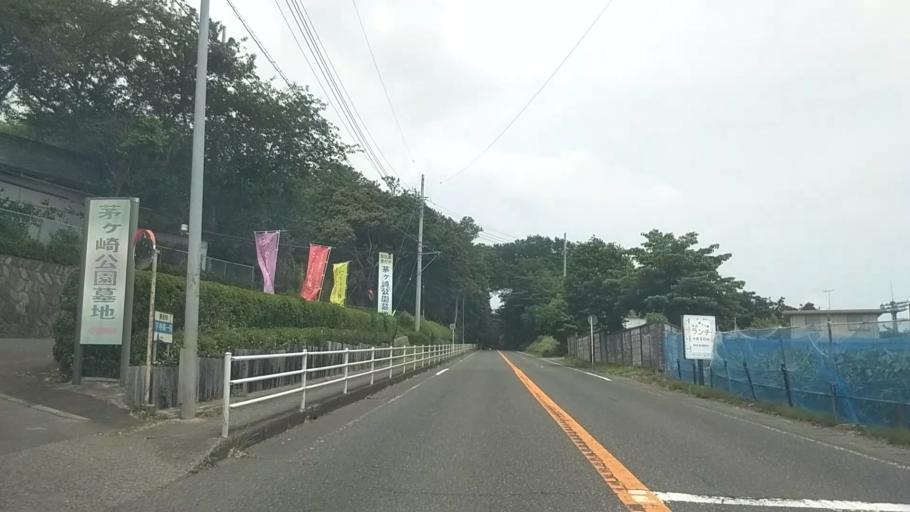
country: JP
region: Kanagawa
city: Chigasaki
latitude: 35.3673
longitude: 139.4065
